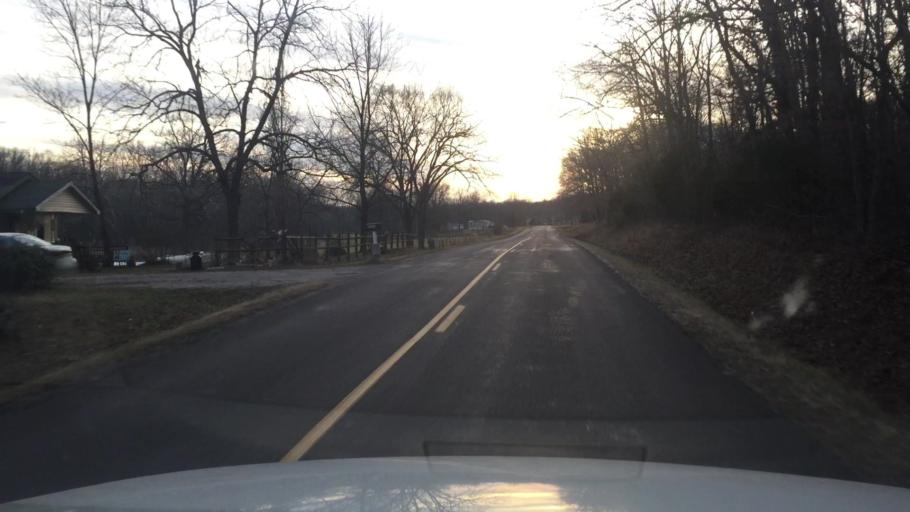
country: US
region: Missouri
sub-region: Miller County
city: Eldon
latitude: 38.3517
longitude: -92.6983
